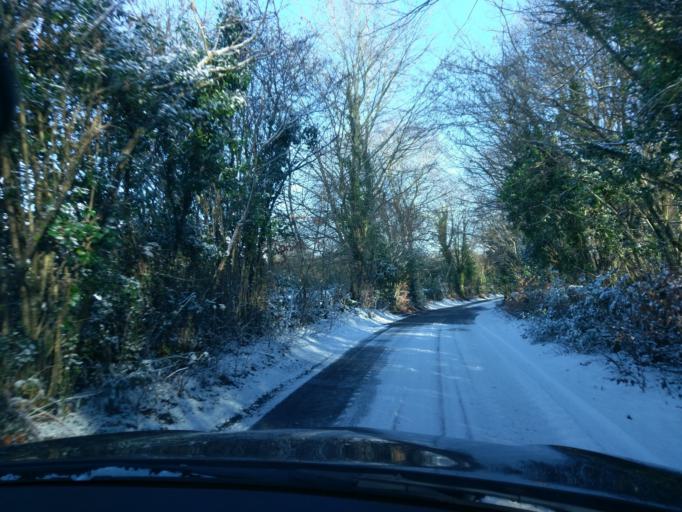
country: IE
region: Connaught
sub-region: County Galway
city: Gort
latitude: 53.1846
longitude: -8.8151
